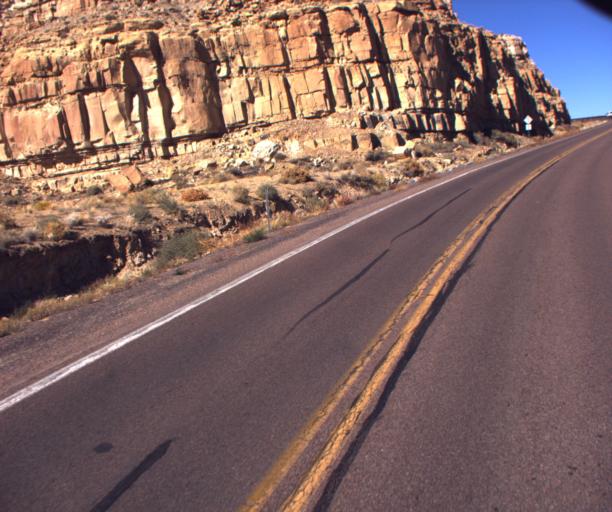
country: US
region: Arizona
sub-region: Navajo County
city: First Mesa
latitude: 35.8070
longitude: -110.5215
